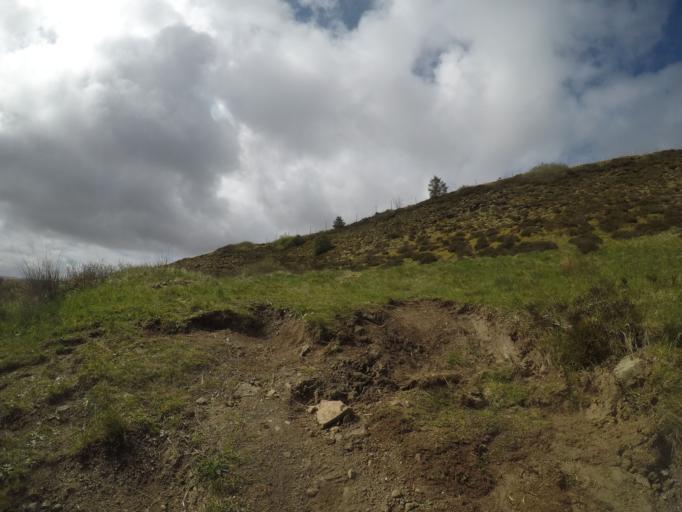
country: GB
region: Scotland
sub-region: Highland
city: Portree
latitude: 57.4975
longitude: -6.1594
